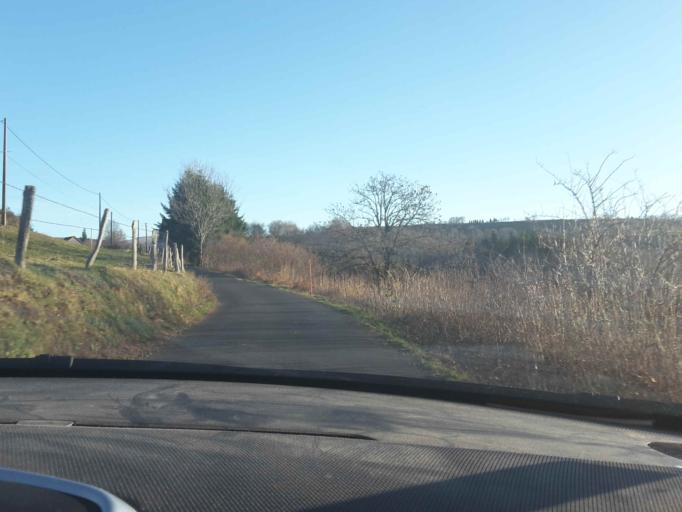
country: FR
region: Auvergne
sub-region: Departement du Cantal
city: Ydes
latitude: 45.2376
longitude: 2.5470
